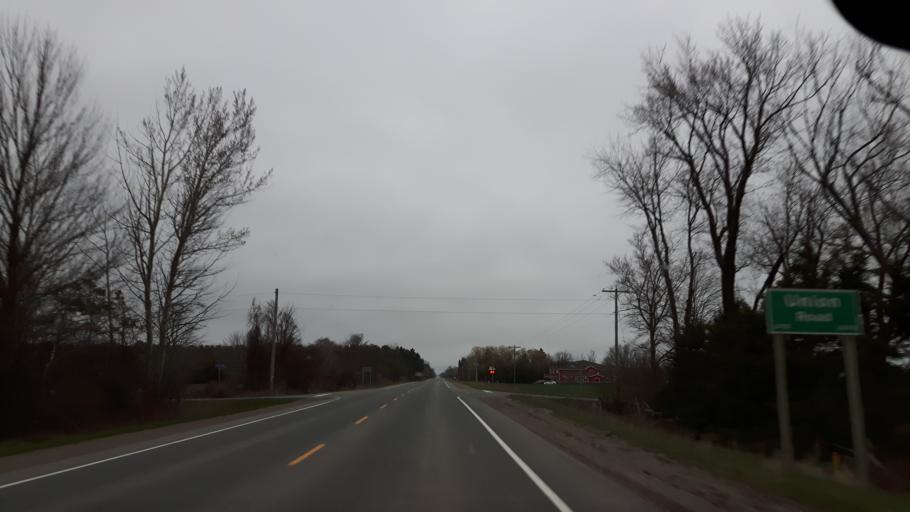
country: CA
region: Ontario
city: Goderich
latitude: 43.6803
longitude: -81.7057
